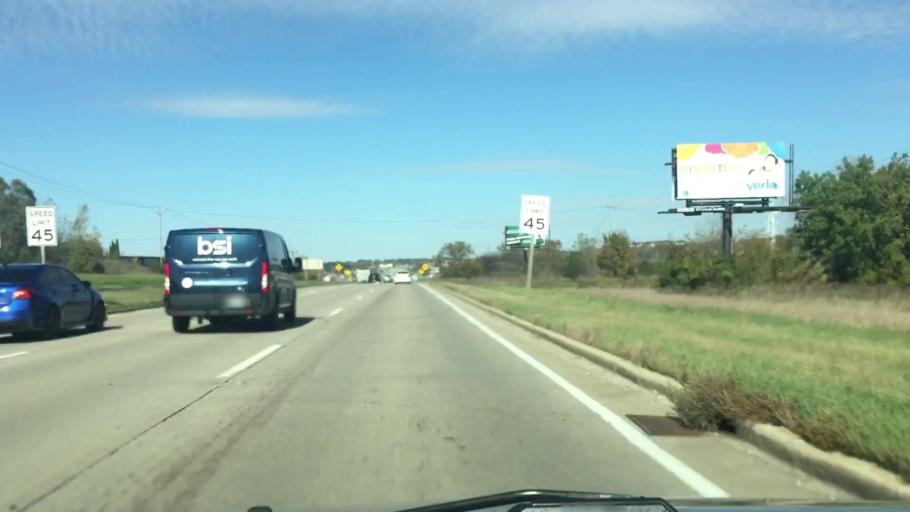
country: US
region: Wisconsin
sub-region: Waukesha County
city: Waukesha
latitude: 43.0038
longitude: -88.1992
